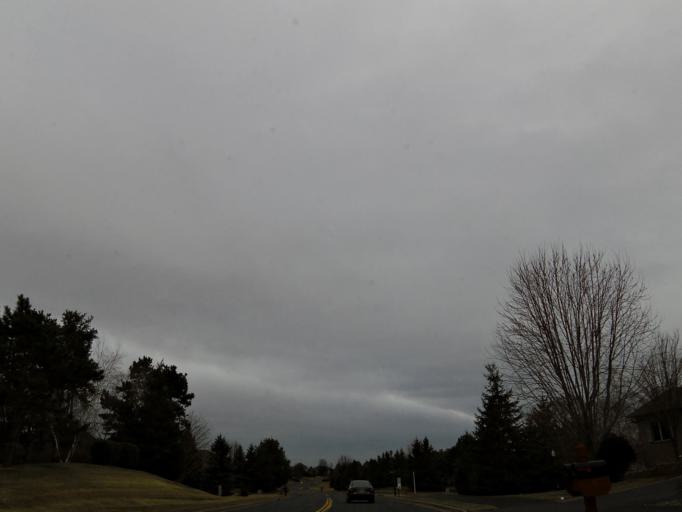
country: US
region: Wisconsin
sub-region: Saint Croix County
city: Hudson
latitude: 44.9768
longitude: -92.7306
